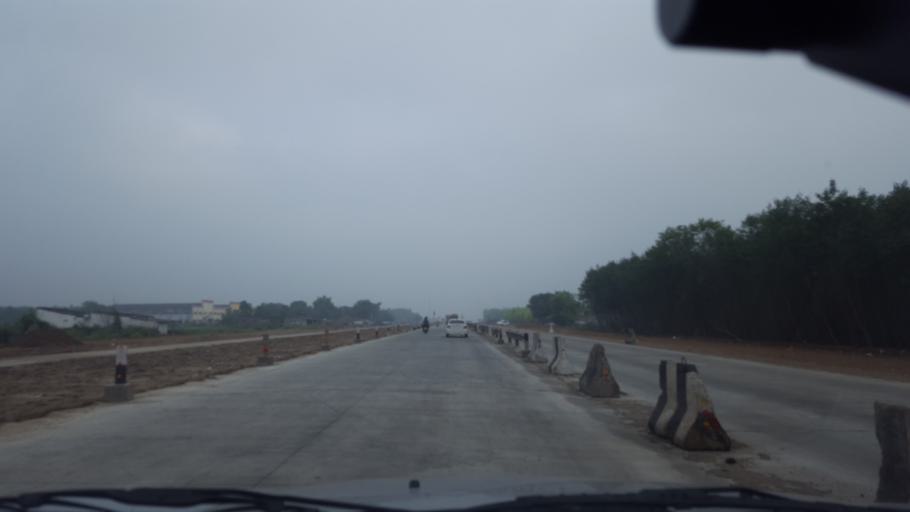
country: IN
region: Andhra Pradesh
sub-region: Prakasam
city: Addanki
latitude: 15.7913
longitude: 80.0382
